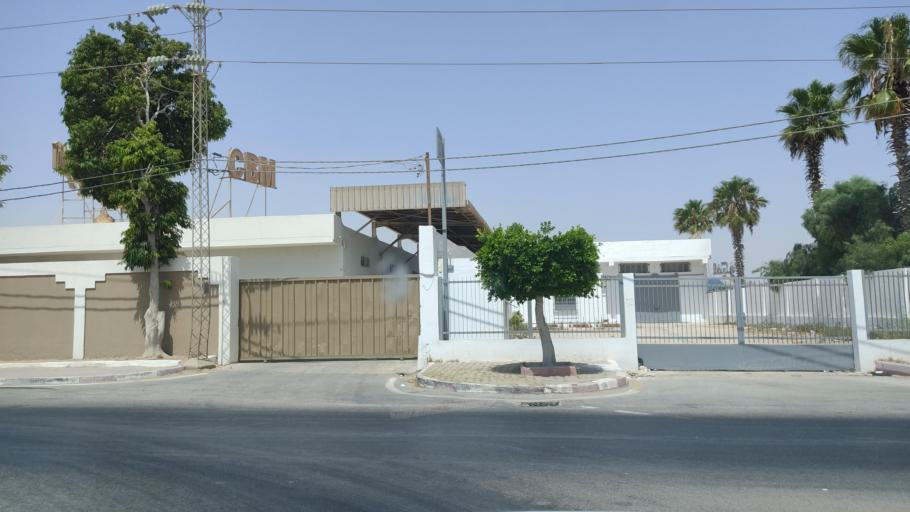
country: TN
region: Safaqis
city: Sfax
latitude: 34.6996
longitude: 10.7185
